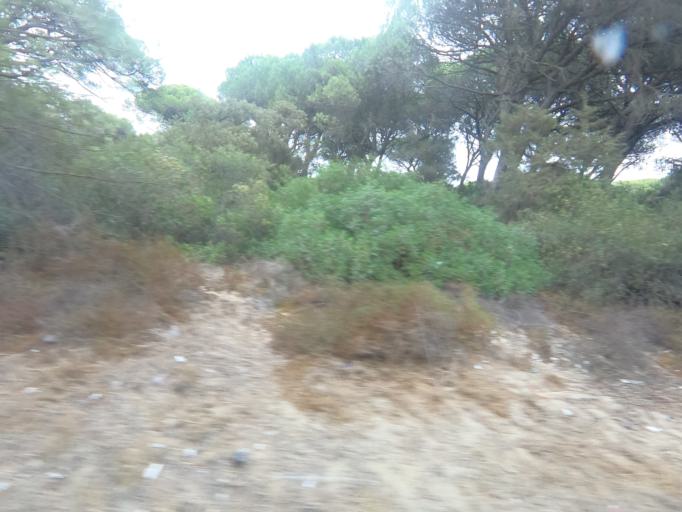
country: PT
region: Setubal
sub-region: Almada
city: Charneca
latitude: 38.6010
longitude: -9.1952
